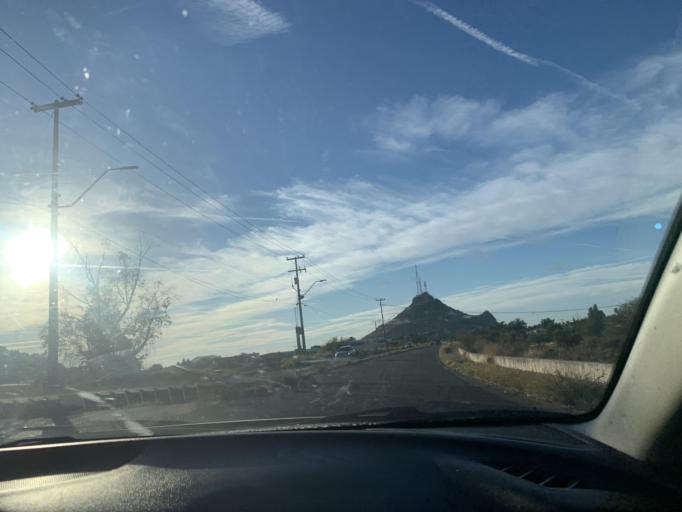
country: MX
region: Sonora
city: Hermosillo
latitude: 29.0721
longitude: -110.9335
